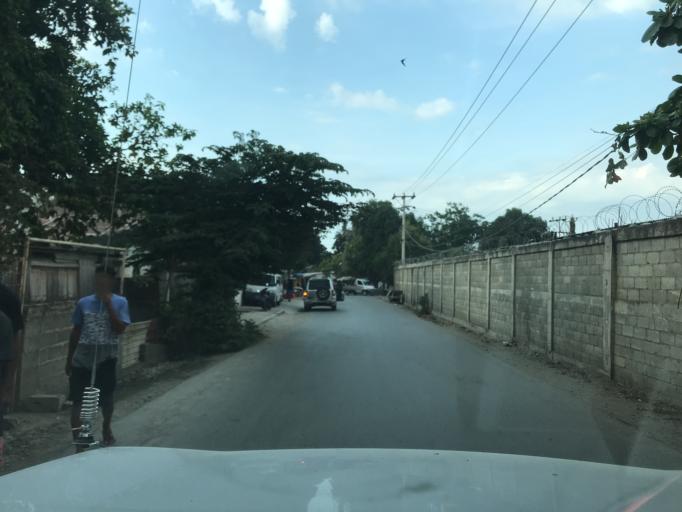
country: TL
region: Dili
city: Dili
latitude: -8.5522
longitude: 125.5401
